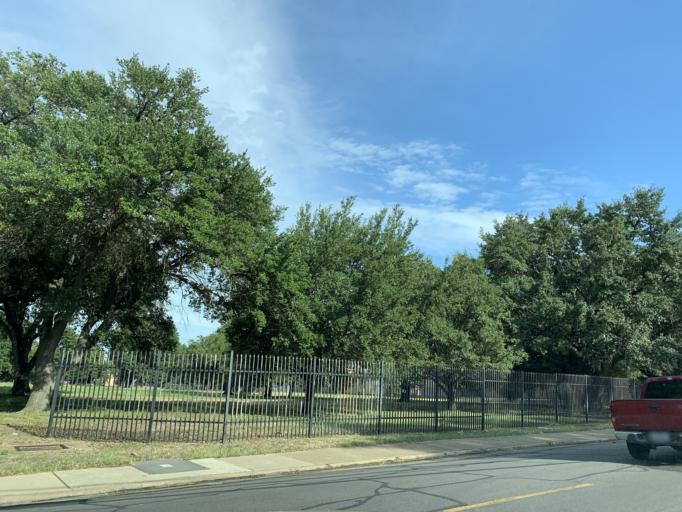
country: US
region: Texas
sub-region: Dallas County
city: Dallas
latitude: 32.7392
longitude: -96.8322
